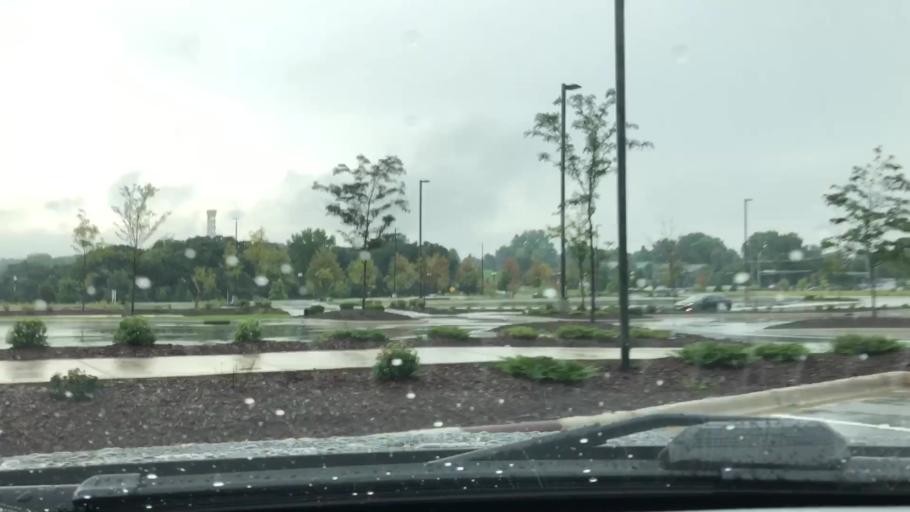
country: US
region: Minnesota
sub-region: Dakota County
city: Eagan
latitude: 44.8368
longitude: -93.1694
